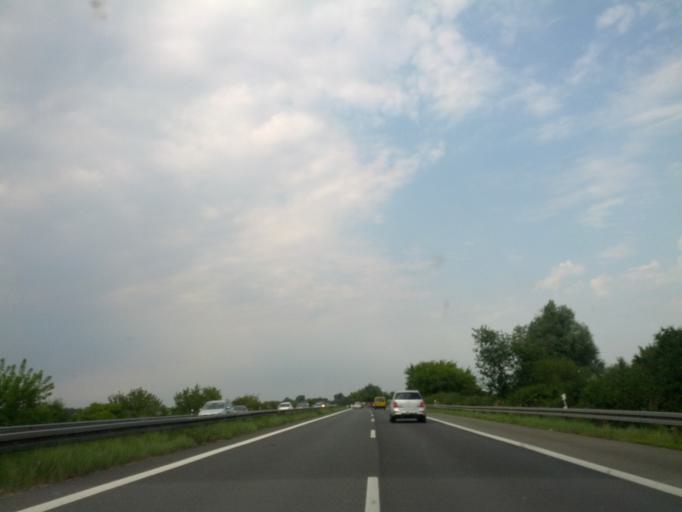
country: DE
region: Brandenburg
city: Fehrbellin
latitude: 52.8230
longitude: 12.7943
